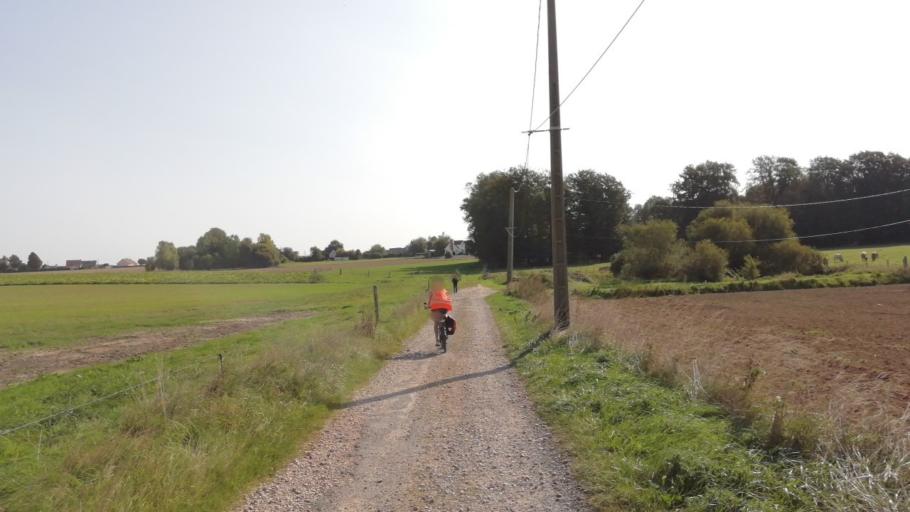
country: FR
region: Haute-Normandie
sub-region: Departement de la Seine-Maritime
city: La Remuee
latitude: 49.5291
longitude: 0.3957
